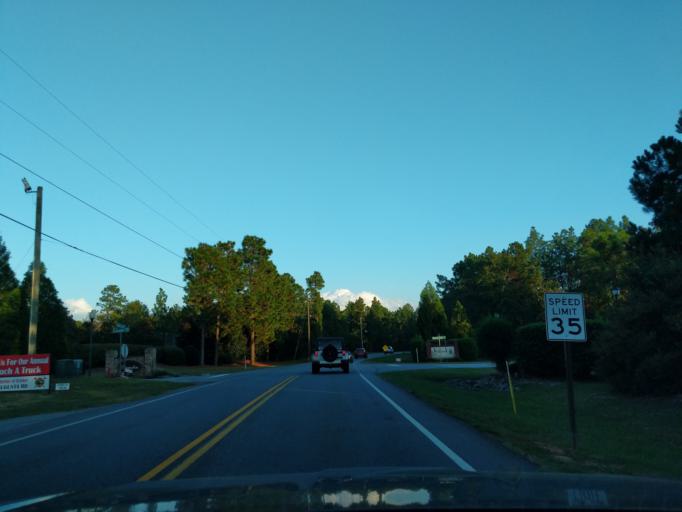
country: US
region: South Carolina
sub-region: Aiken County
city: Burnettown
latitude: 33.5366
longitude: -81.8637
